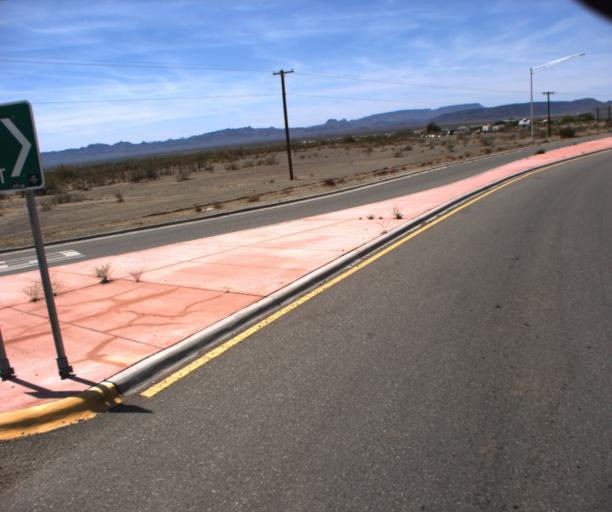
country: US
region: Arizona
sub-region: La Paz County
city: Salome
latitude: 33.7185
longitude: -113.7675
